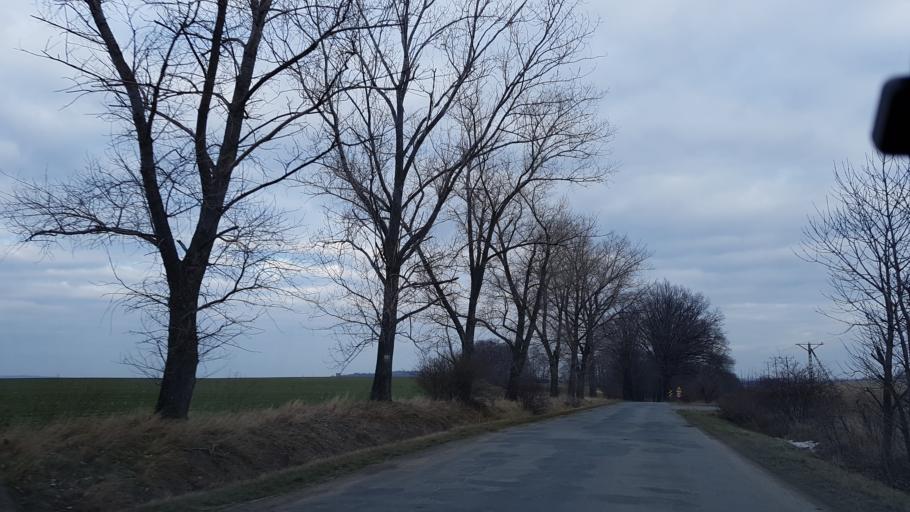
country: PL
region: Lower Silesian Voivodeship
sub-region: Powiat zabkowicki
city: Kamieniec Zabkowicki
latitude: 50.5014
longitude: 16.8505
